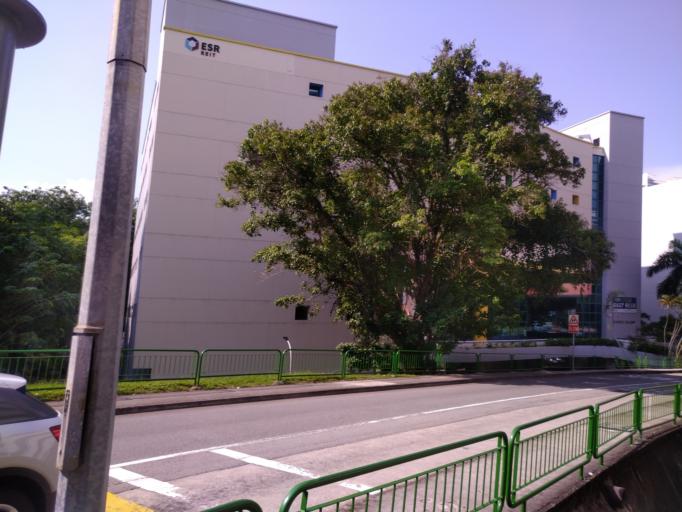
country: SG
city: Singapore
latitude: 1.2879
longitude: 103.8111
